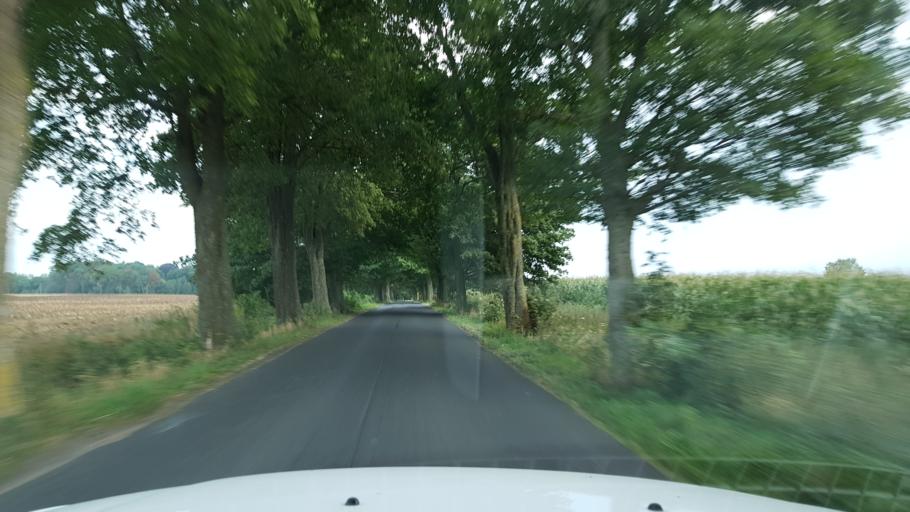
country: PL
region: West Pomeranian Voivodeship
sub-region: Powiat koszalinski
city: Mielno
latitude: 54.2326
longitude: 16.0190
